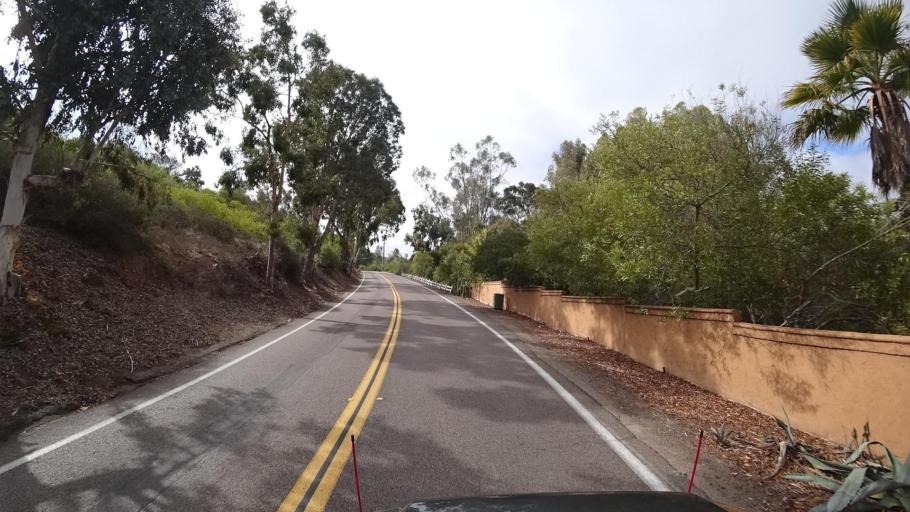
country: US
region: California
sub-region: San Diego County
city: Rancho Santa Fe
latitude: 33.0198
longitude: -117.2411
